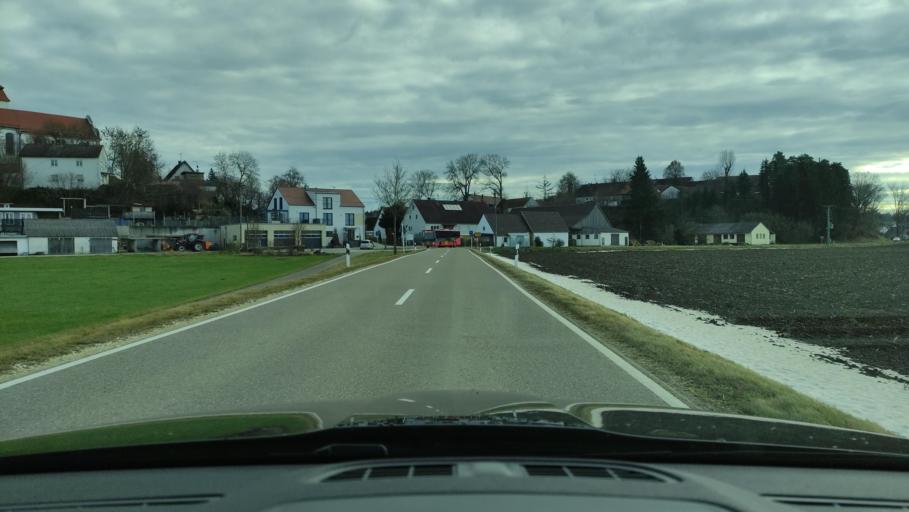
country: DE
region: Bavaria
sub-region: Swabia
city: Deisenhausen
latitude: 48.2828
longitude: 10.3277
